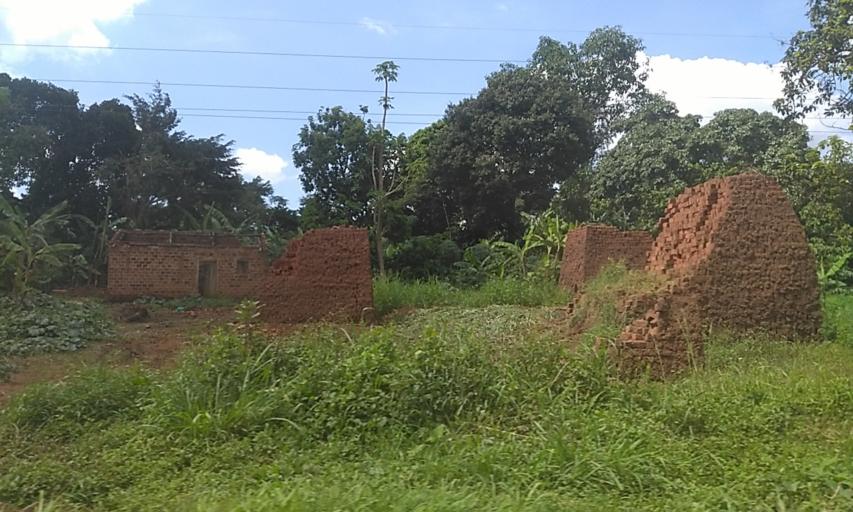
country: UG
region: Central Region
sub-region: Wakiso District
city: Wakiso
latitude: 0.3230
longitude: 32.4543
